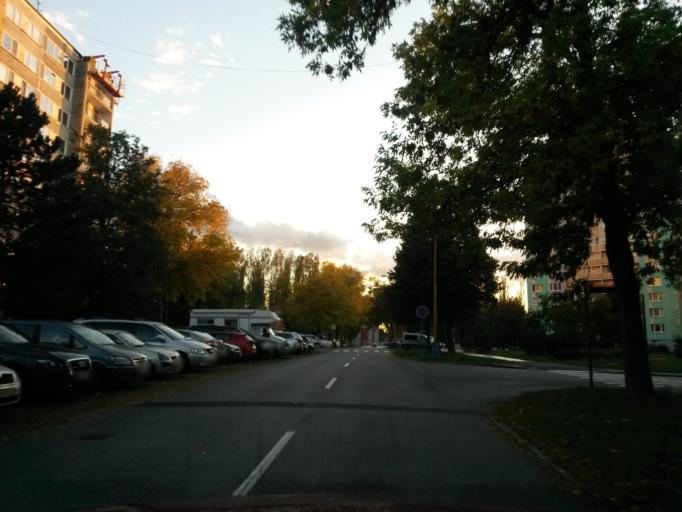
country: SK
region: Kosicky
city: Kosice
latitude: 48.6875
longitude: 21.2872
